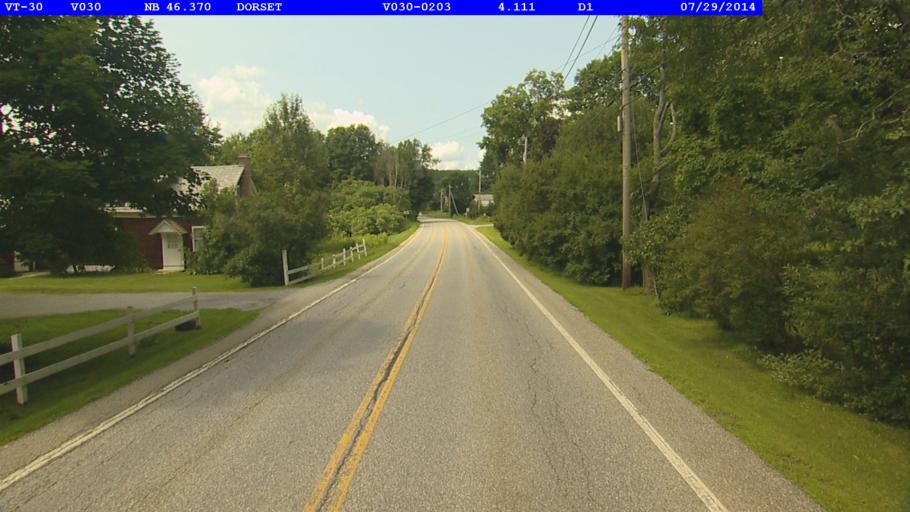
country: US
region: Vermont
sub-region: Bennington County
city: Manchester Center
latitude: 43.2642
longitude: -73.1055
